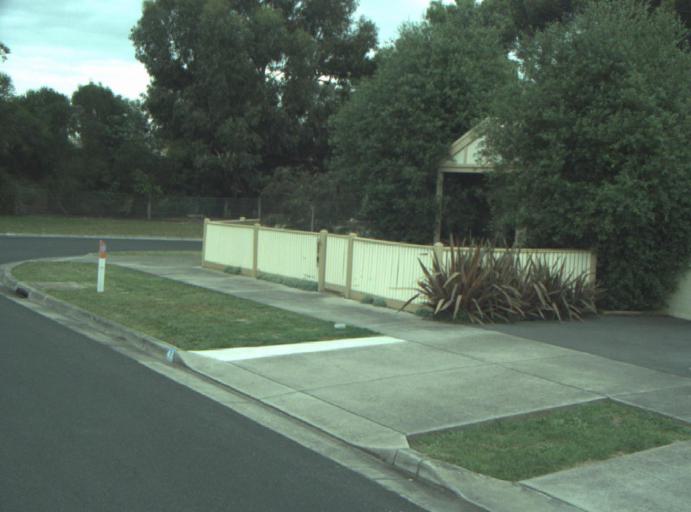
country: AU
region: Victoria
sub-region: Greater Geelong
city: Breakwater
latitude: -38.1929
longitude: 144.3352
